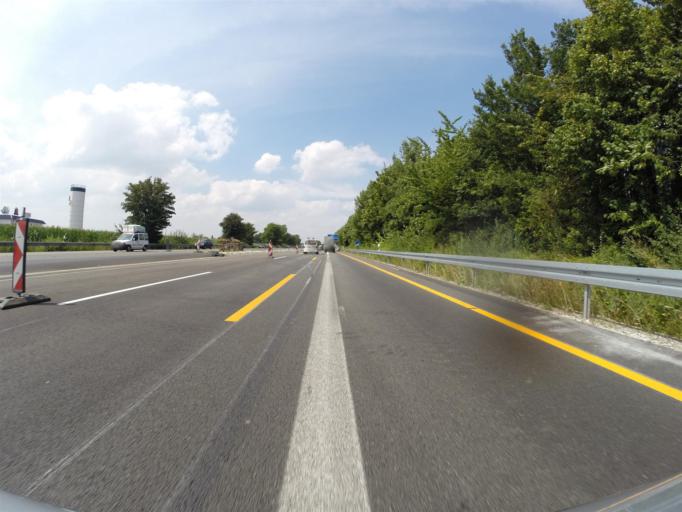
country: DE
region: North Rhine-Westphalia
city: Buende
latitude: 52.1971
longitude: 8.5470
